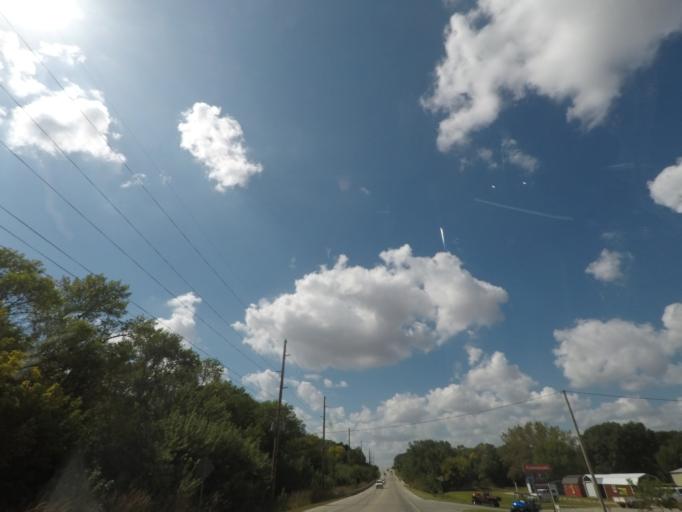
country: US
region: Iowa
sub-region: Story County
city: Nevada
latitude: 42.0228
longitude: -93.4660
